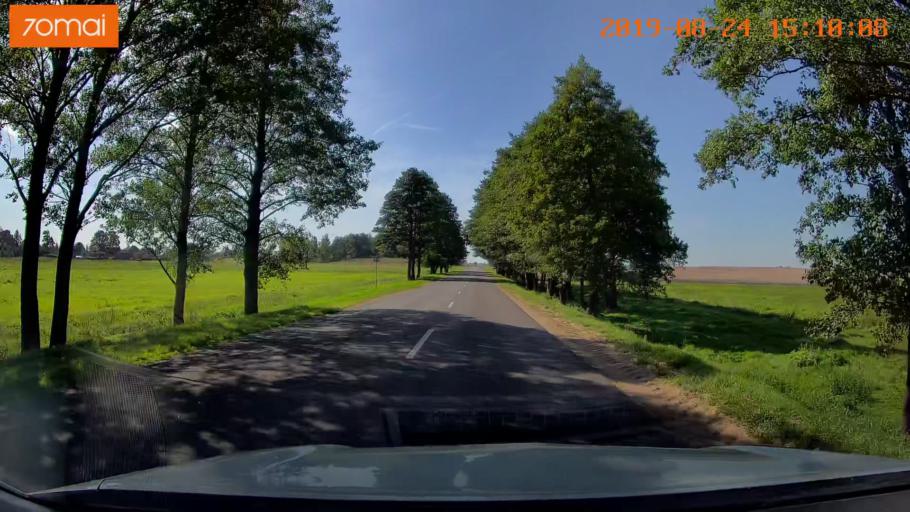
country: BY
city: Michanovichi
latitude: 53.6089
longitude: 27.6273
